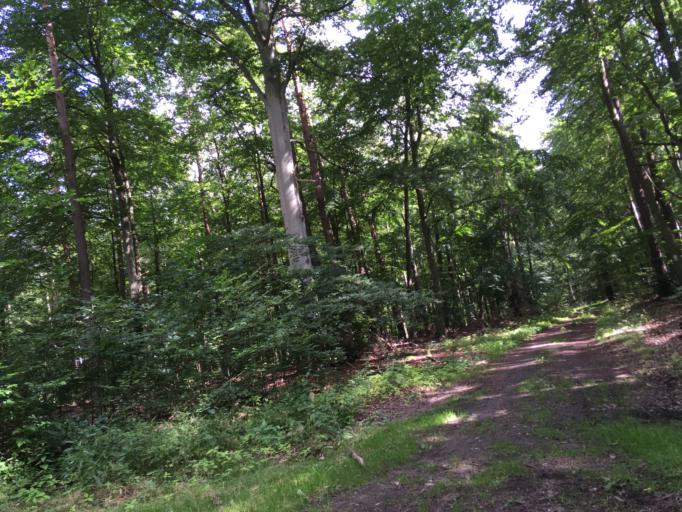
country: DE
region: Brandenburg
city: Bernau bei Berlin
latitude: 52.7230
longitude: 13.5496
